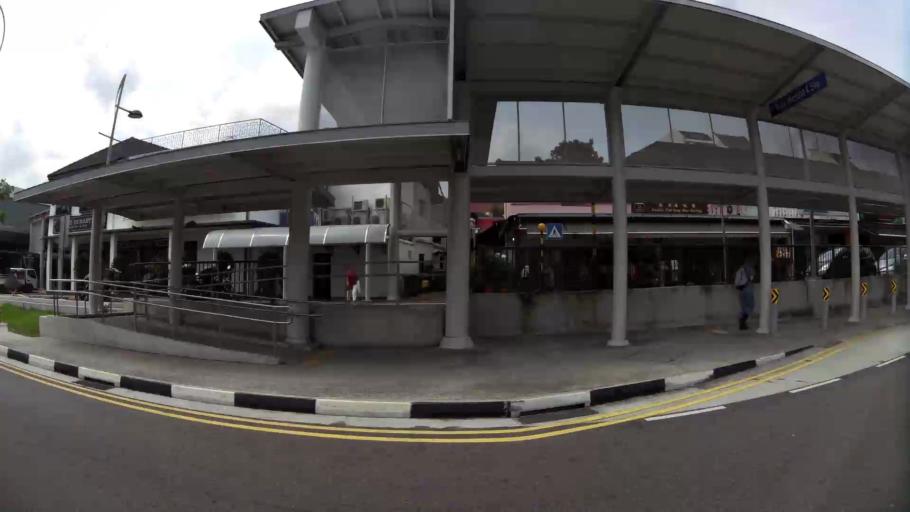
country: SG
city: Singapore
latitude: 1.3424
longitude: 103.7755
